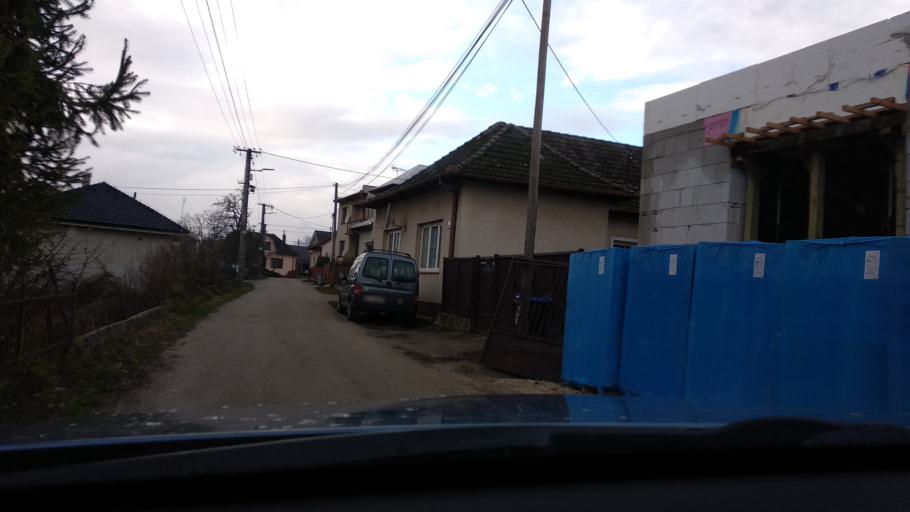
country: SK
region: Trenciansky
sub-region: Okres Trencin
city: Trencin
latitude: 48.8463
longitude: 18.0440
